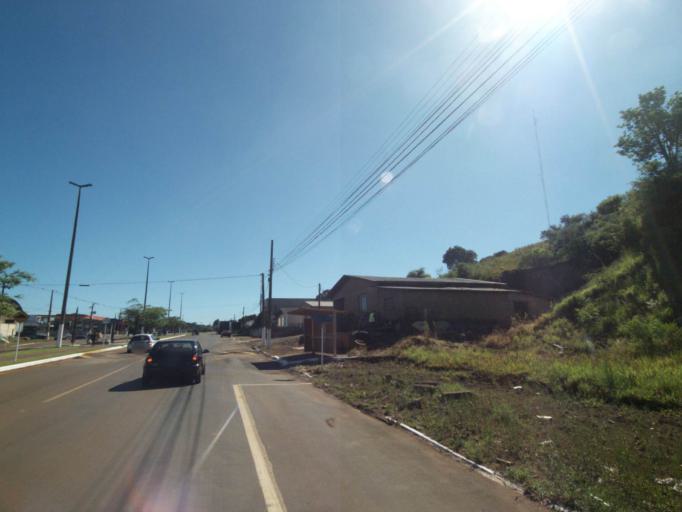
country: BR
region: Parana
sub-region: Pato Branco
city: Pato Branco
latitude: -26.2604
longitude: -52.7751
